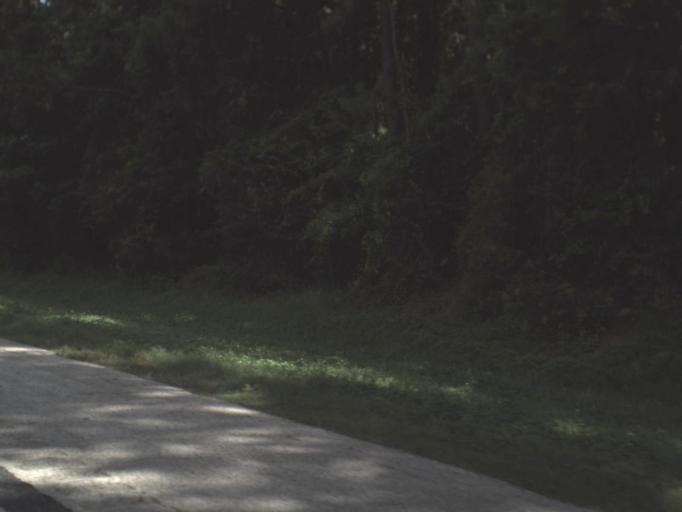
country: US
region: Florida
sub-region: Alachua County
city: High Springs
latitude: 29.8189
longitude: -82.5166
